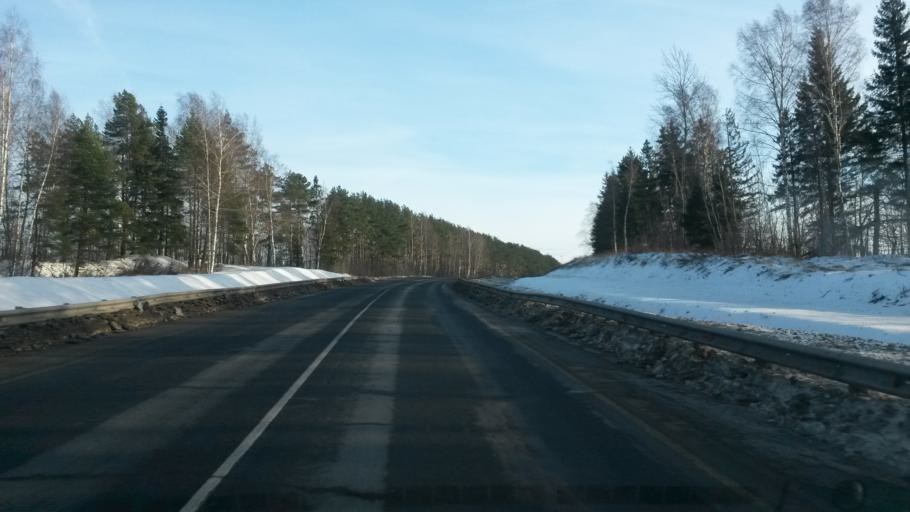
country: RU
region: Jaroslavl
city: Levashevo
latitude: 57.6438
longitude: 40.5070
